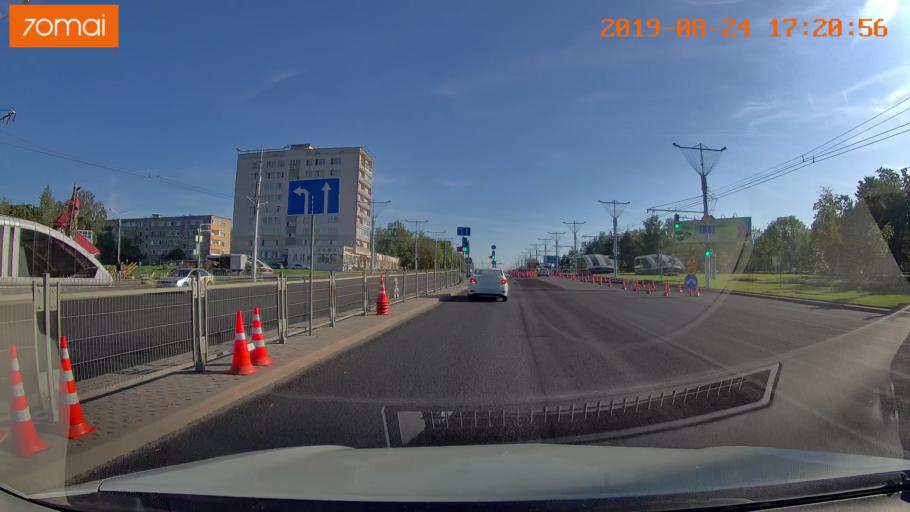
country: BY
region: Minsk
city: Hatava
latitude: 53.8499
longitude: 27.6338
